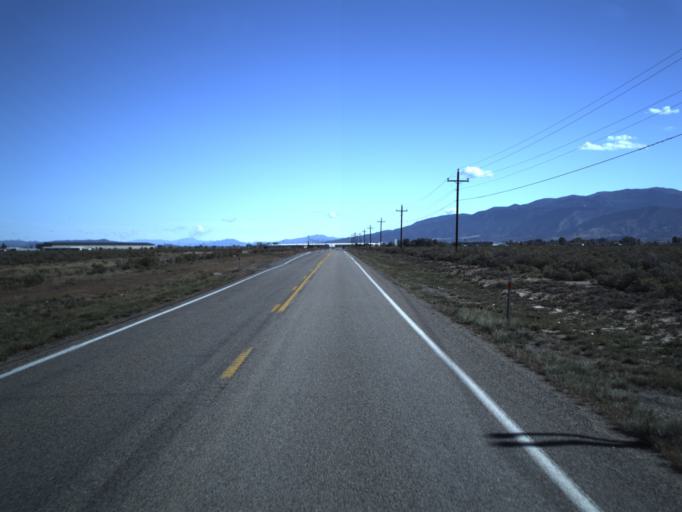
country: US
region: Utah
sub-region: Iron County
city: Cedar City
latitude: 37.6766
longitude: -113.1791
